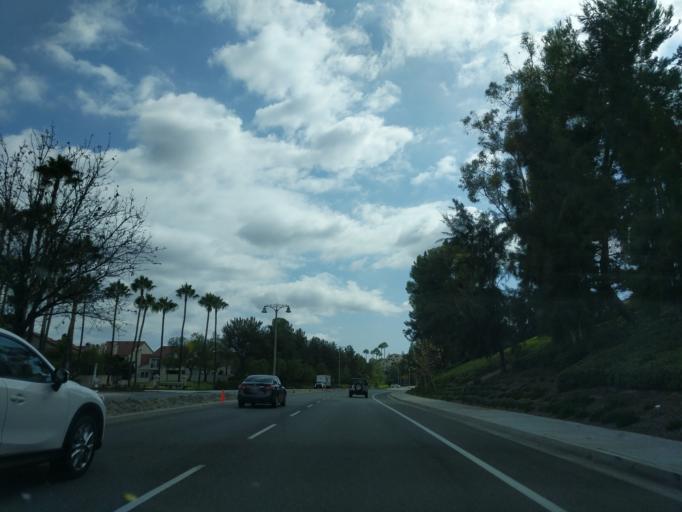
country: US
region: California
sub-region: Orange County
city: Portola Hills
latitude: 33.6435
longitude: -117.6436
